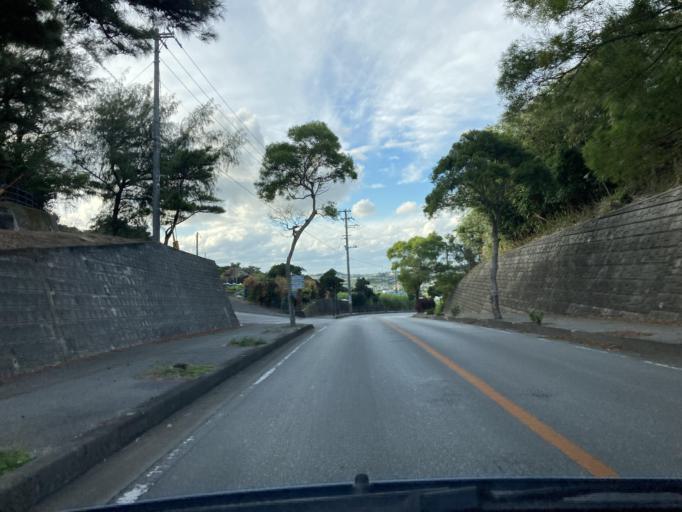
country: JP
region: Okinawa
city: Itoman
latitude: 26.1322
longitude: 127.7236
